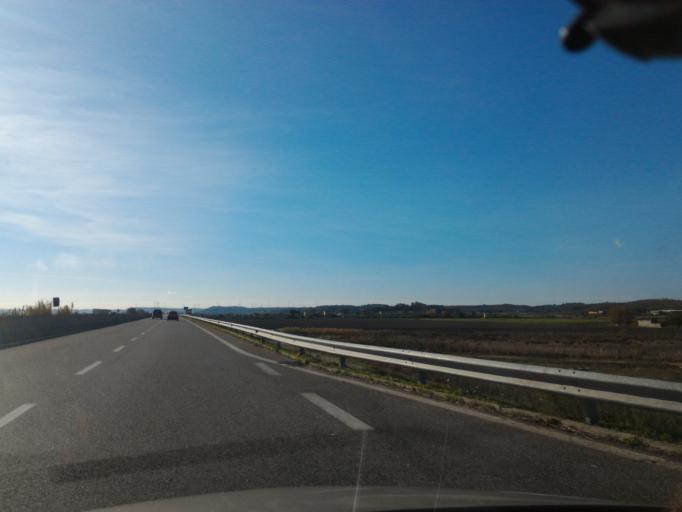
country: IT
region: Calabria
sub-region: Provincia di Crotone
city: Crotone
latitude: 39.1529
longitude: 17.0970
